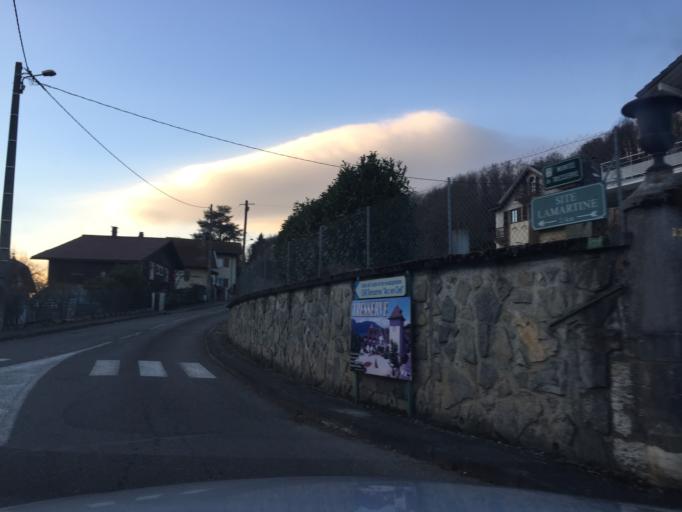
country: FR
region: Rhone-Alpes
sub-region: Departement de la Savoie
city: Tresserve
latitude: 45.6856
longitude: 5.9042
